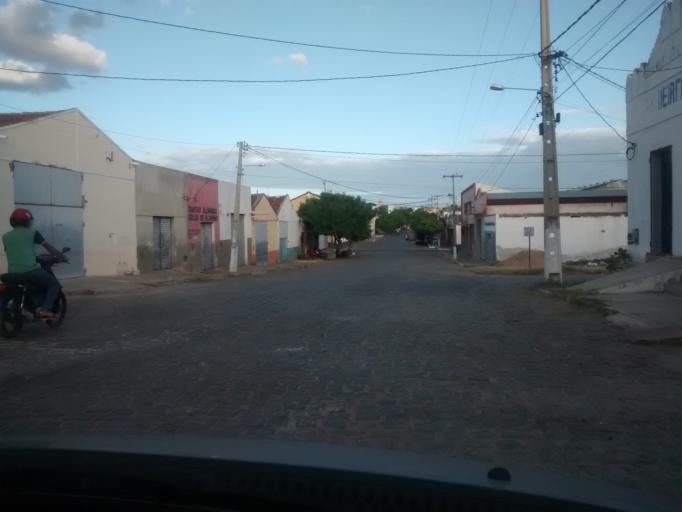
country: BR
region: Rio Grande do Norte
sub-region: Caico
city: Caico
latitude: -6.4626
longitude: -37.0993
